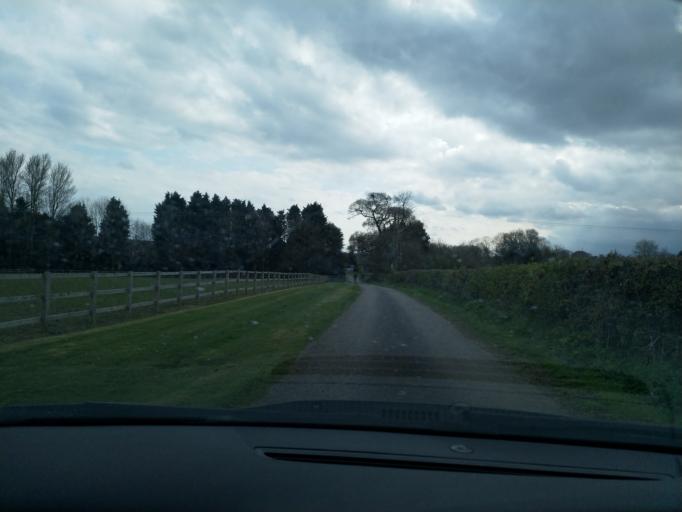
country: GB
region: England
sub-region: Warwickshire
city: Wroxall
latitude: 52.2918
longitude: -1.6881
